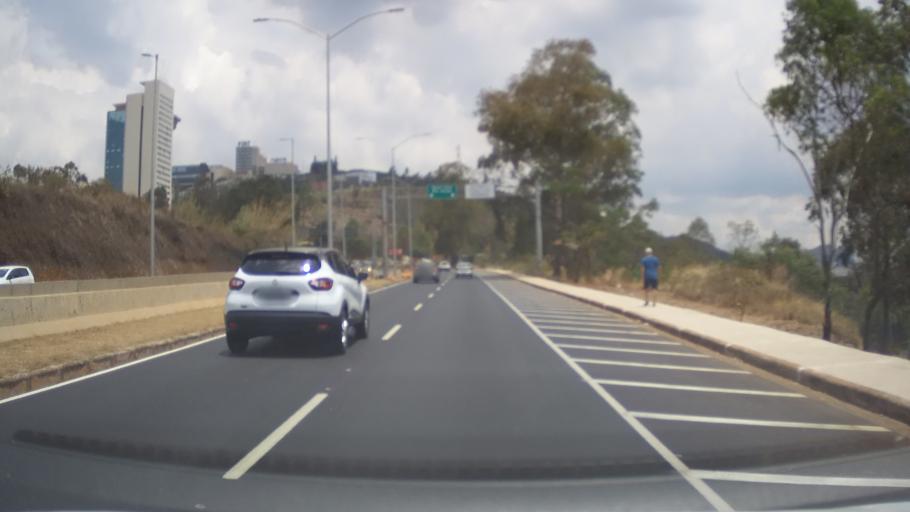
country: BR
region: Minas Gerais
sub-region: Belo Horizonte
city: Belo Horizonte
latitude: -19.9798
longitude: -43.9482
